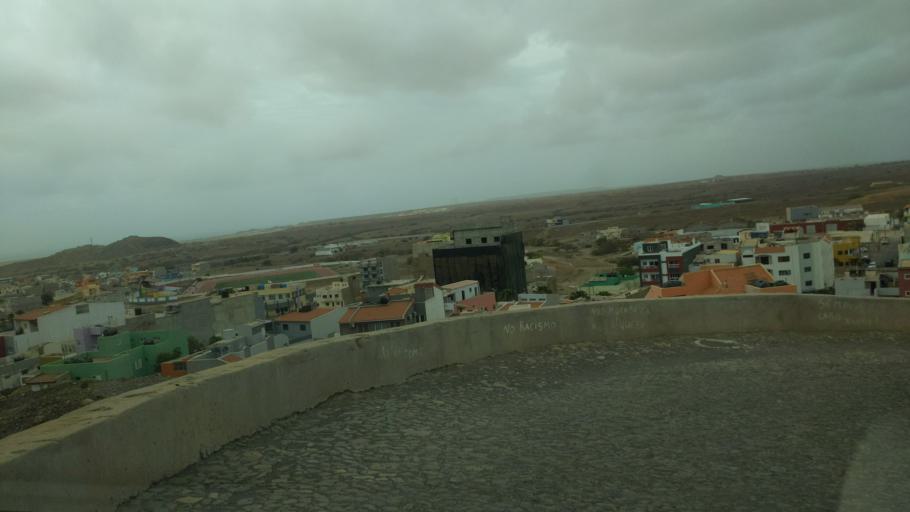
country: CV
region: Sal
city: Espargos
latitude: 16.7563
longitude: -22.9427
